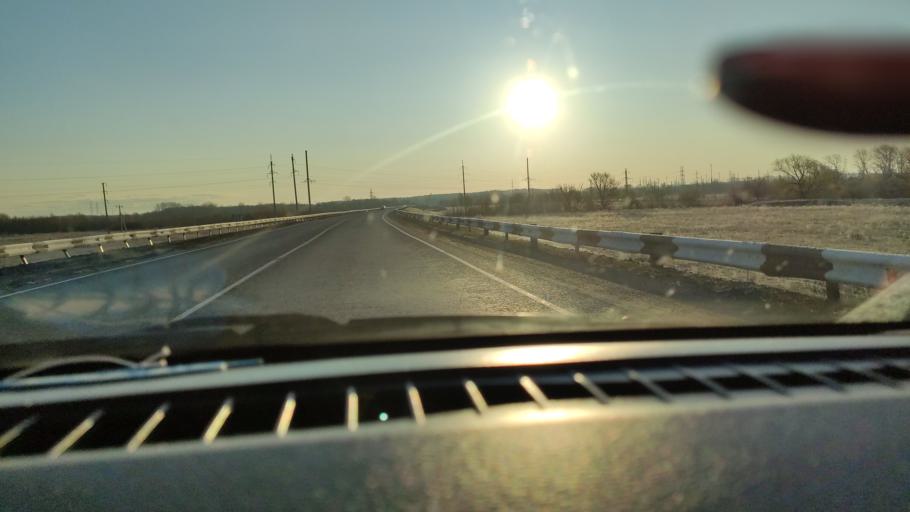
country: RU
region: Saratov
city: Sennoy
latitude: 52.1415
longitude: 46.8909
